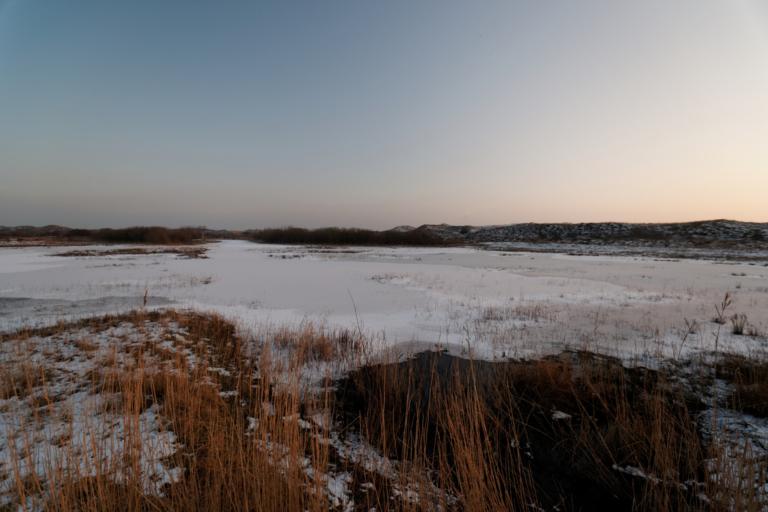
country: NL
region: North Holland
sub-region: Gemeente Texel
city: Den Burg
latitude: 53.1090
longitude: 4.7791
